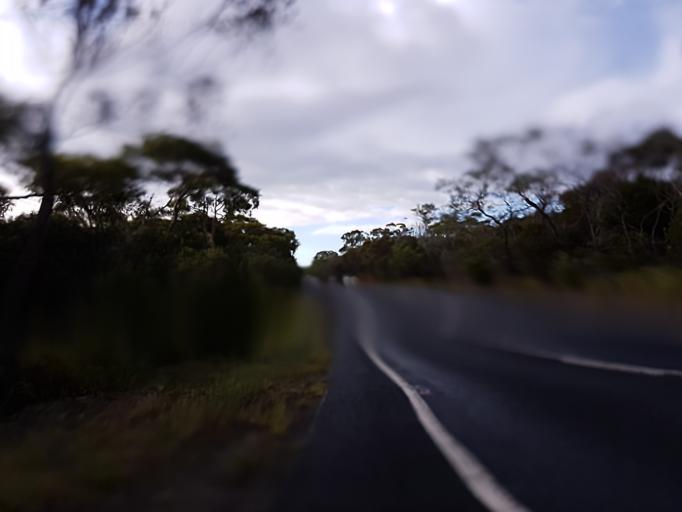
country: AU
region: New South Wales
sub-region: Warringah
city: Killarney Heights
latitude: -33.7635
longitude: 151.2326
